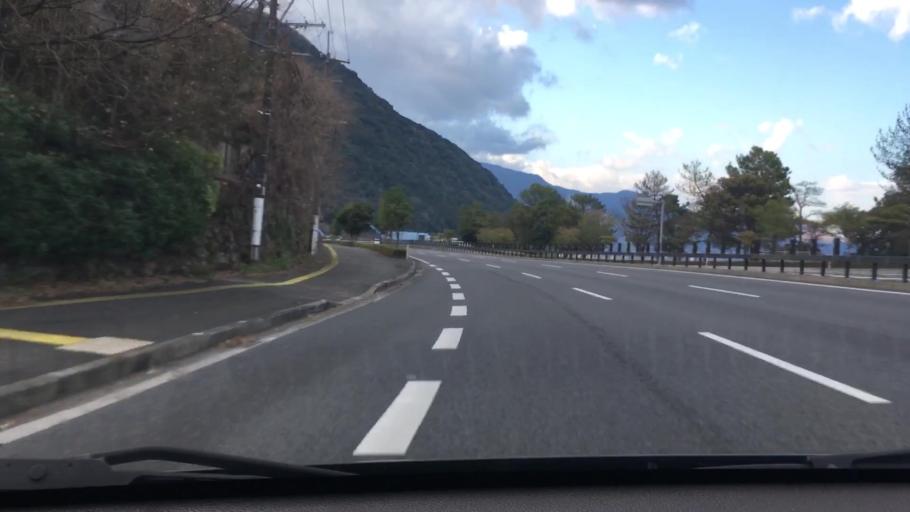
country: JP
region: Oita
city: Beppu
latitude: 33.2565
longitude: 131.5436
